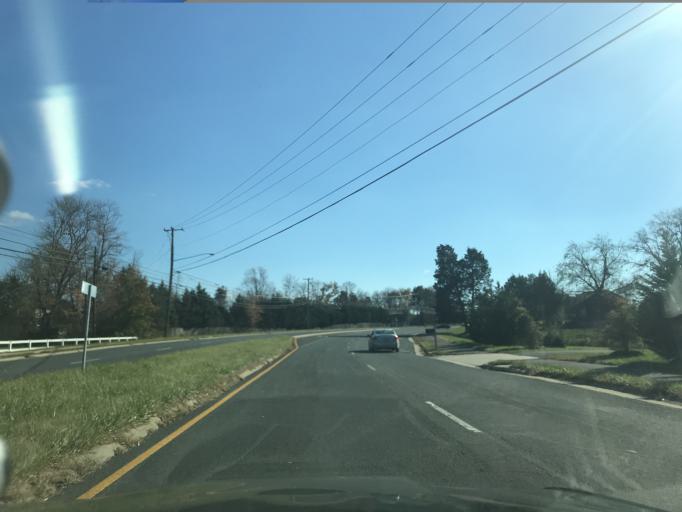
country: US
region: Virginia
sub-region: Fairfax County
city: Oak Hill
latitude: 38.9011
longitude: -77.3818
